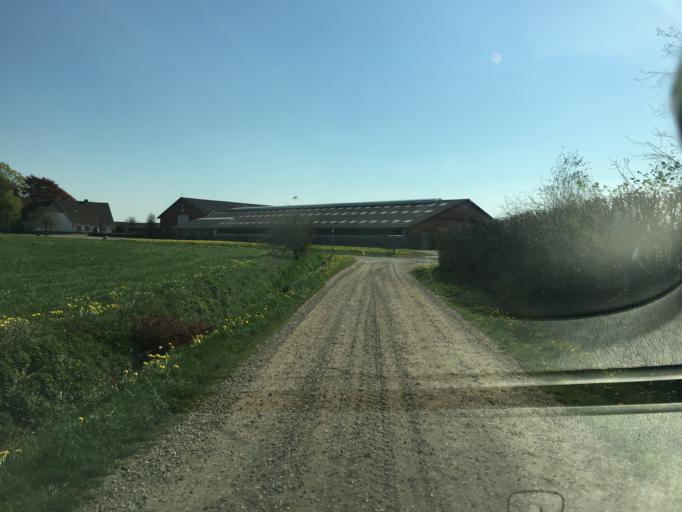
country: DK
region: South Denmark
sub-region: Tonder Kommune
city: Toftlund
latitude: 55.1592
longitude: 9.0915
